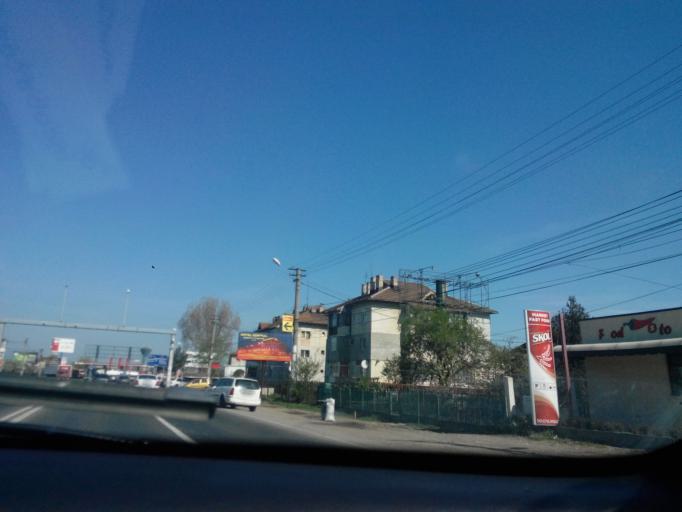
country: RO
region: Prahova
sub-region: Comuna Barcanesti
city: Barcanesti
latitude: 44.8833
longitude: 26.0480
